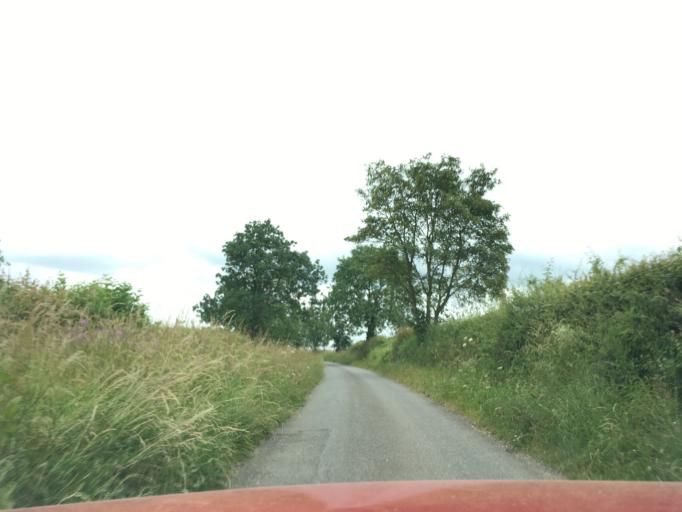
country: GB
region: England
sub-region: Oxfordshire
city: Charlbury
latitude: 51.9129
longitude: -1.5061
